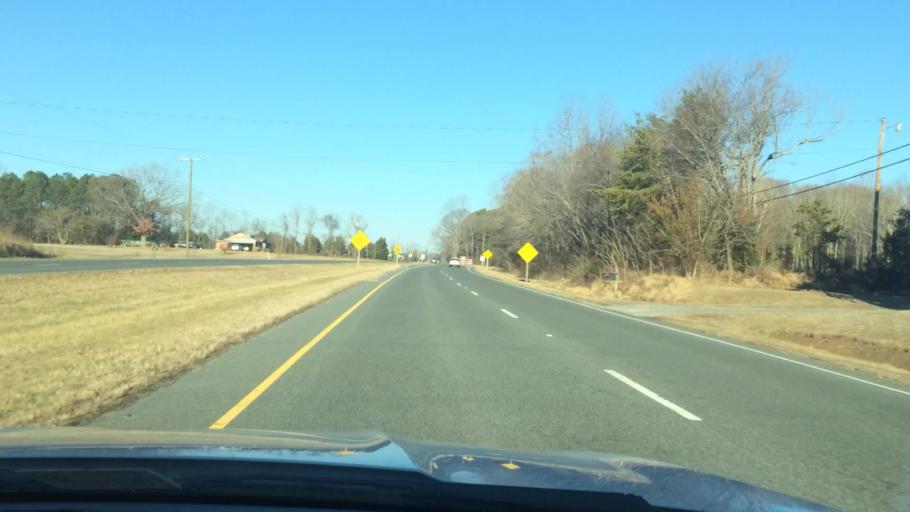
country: US
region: Virginia
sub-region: Lancaster County
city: Kilmarnock
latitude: 37.7479
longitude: -76.4041
